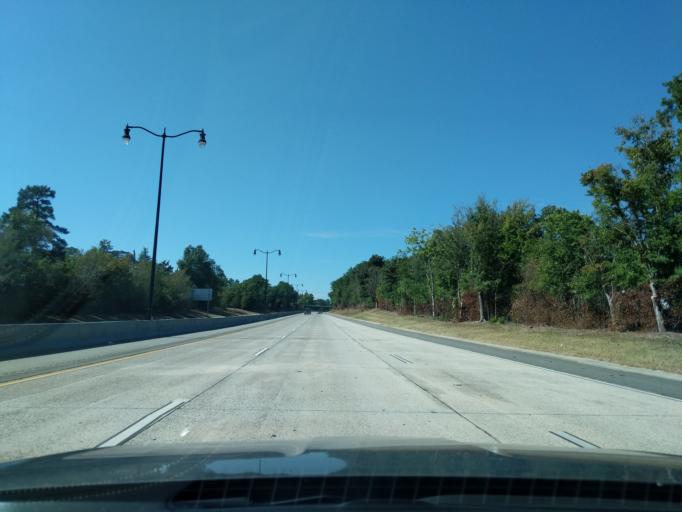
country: US
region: Georgia
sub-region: Richmond County
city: Augusta
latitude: 33.4850
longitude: -82.0009
